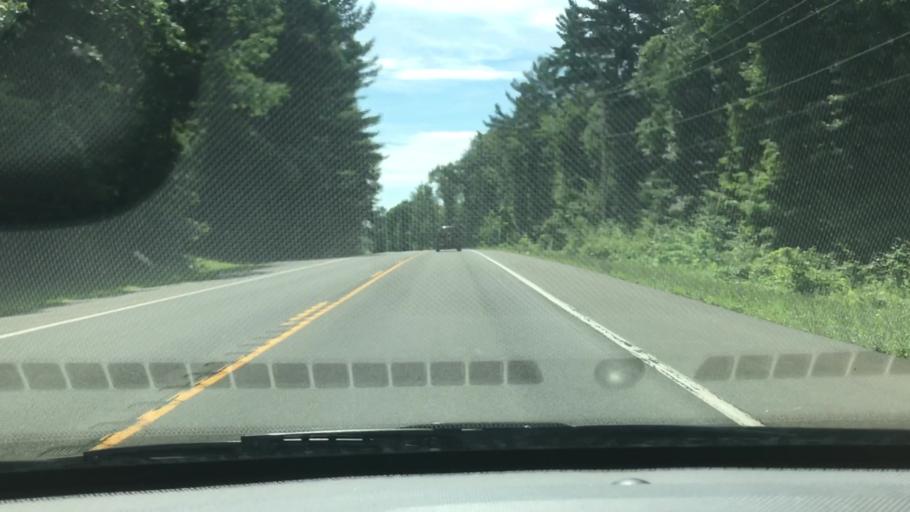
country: US
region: New York
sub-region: Ulster County
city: Shokan
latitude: 41.9797
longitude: -74.2519
